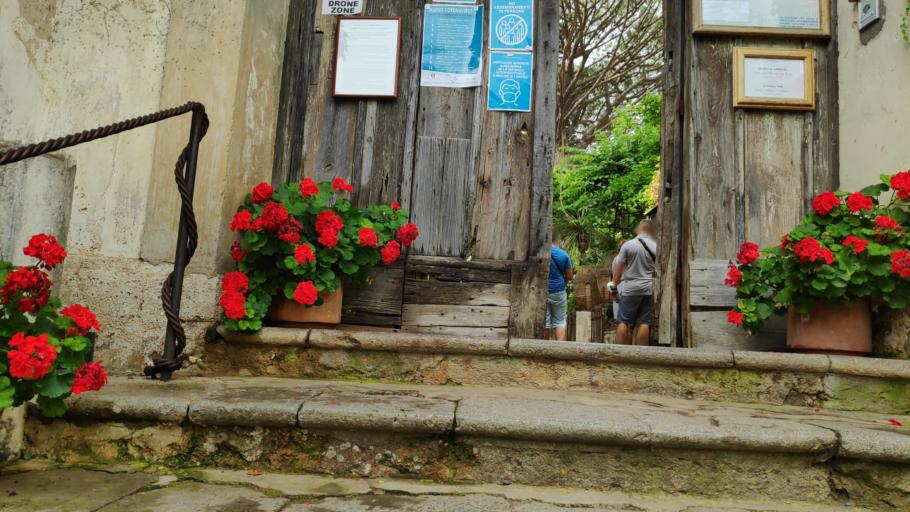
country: IT
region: Campania
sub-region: Provincia di Salerno
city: Ravello
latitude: 40.6445
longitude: 14.6109
